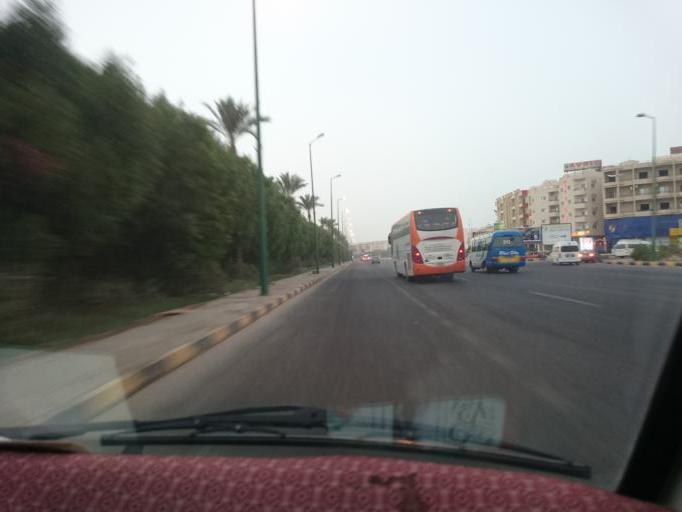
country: EG
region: Red Sea
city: Hurghada
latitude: 27.1995
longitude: 33.8221
